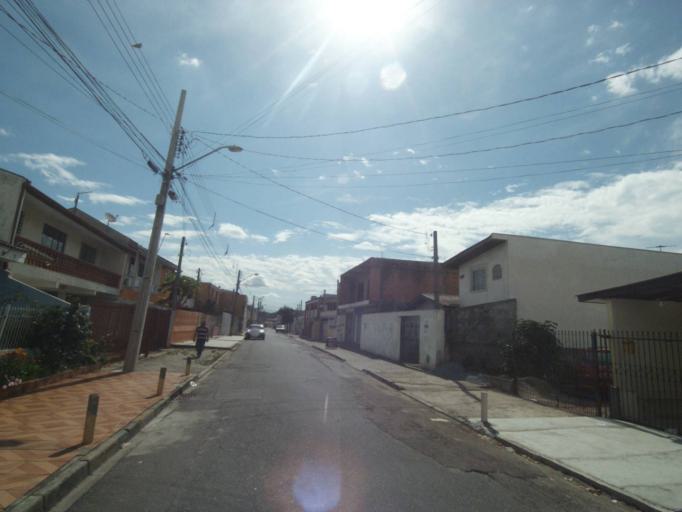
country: BR
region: Parana
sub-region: Curitiba
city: Curitiba
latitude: -25.5160
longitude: -49.3296
